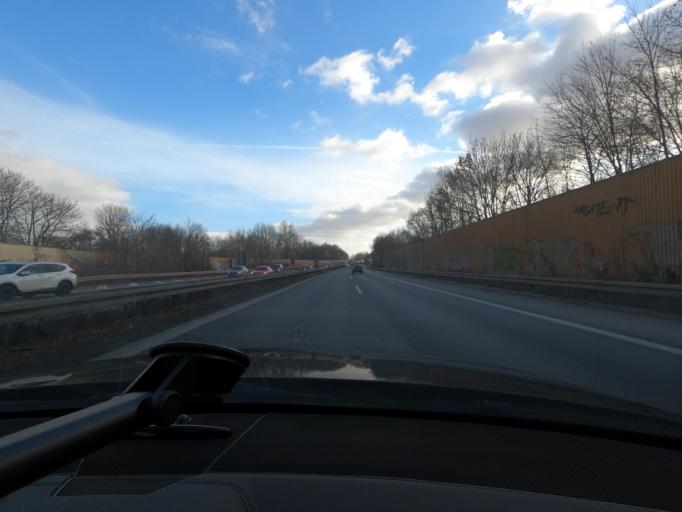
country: DE
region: North Rhine-Westphalia
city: Lanstrop
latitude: 51.5584
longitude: 7.5122
